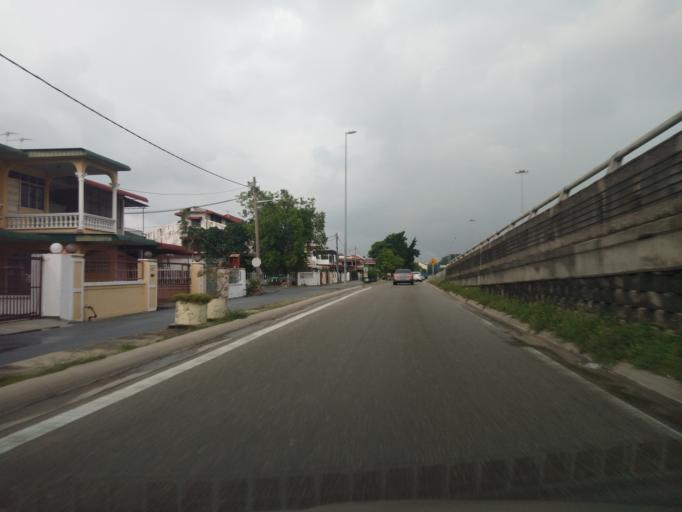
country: MY
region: Penang
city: Permatang Kuching
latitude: 5.4432
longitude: 100.3833
